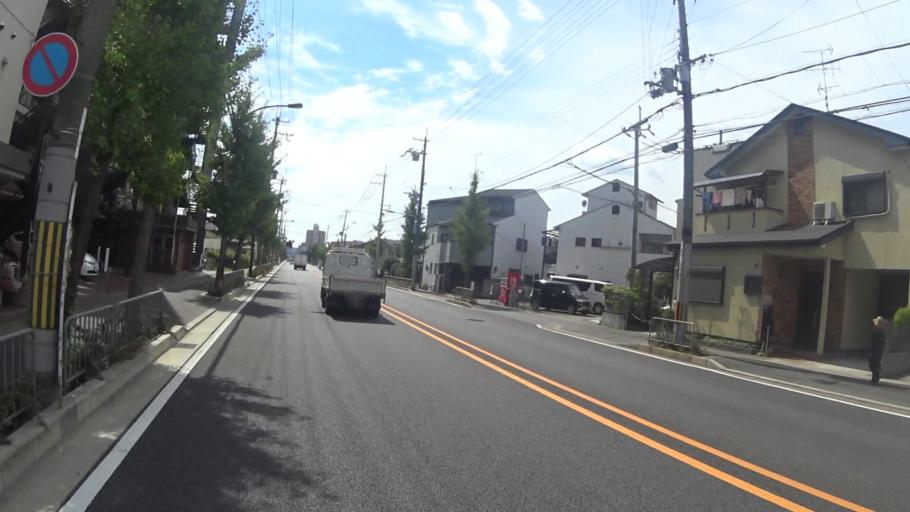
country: JP
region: Kyoto
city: Yawata
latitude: 34.9117
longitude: 135.7229
